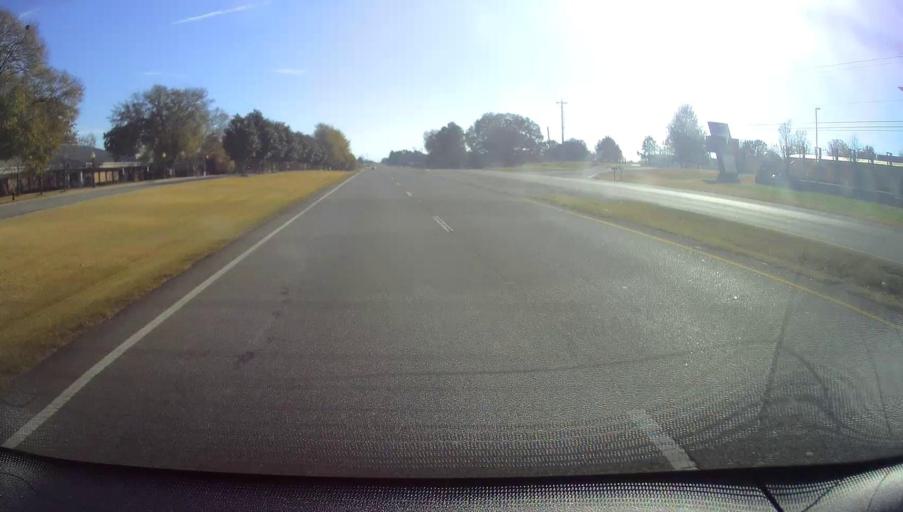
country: US
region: Alabama
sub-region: Morgan County
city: Decatur
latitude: 34.6515
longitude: -86.9504
